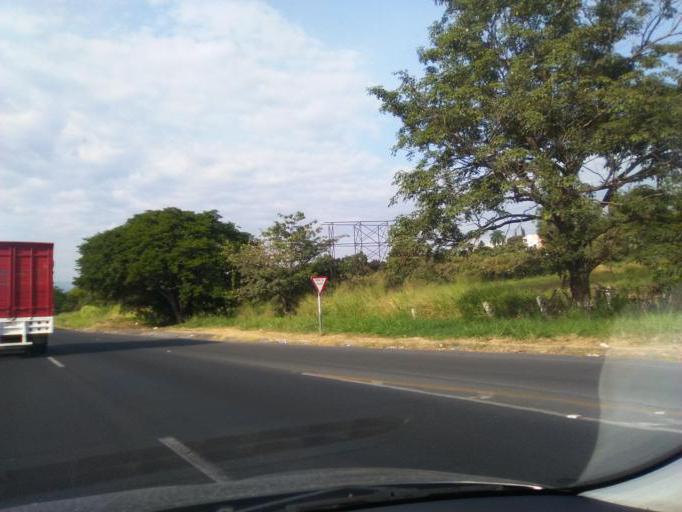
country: MX
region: Morelos
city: Temixco
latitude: 18.8606
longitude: -99.2209
